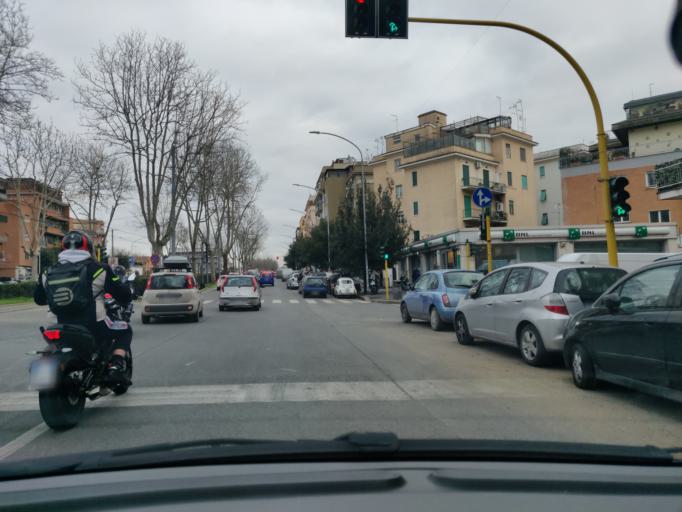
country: VA
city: Vatican City
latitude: 41.8760
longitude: 12.4447
